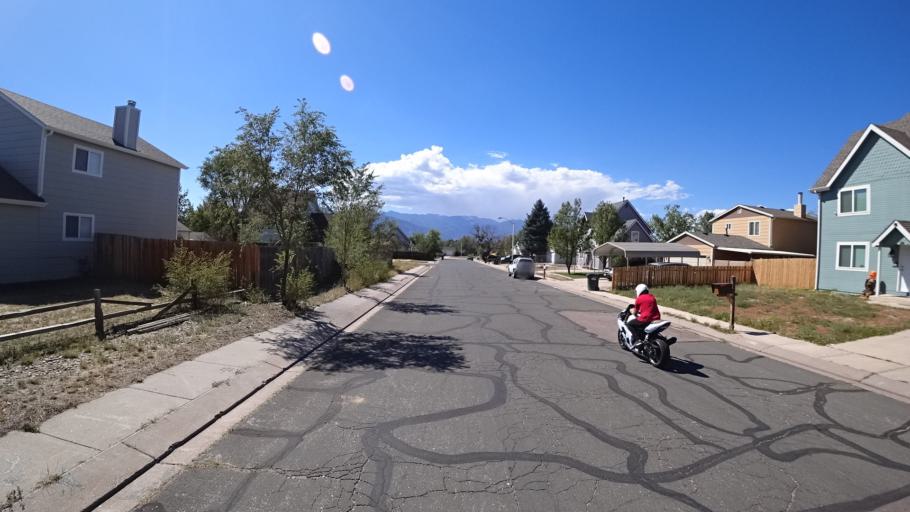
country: US
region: Colorado
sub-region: El Paso County
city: Stratmoor
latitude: 38.7840
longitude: -104.7449
